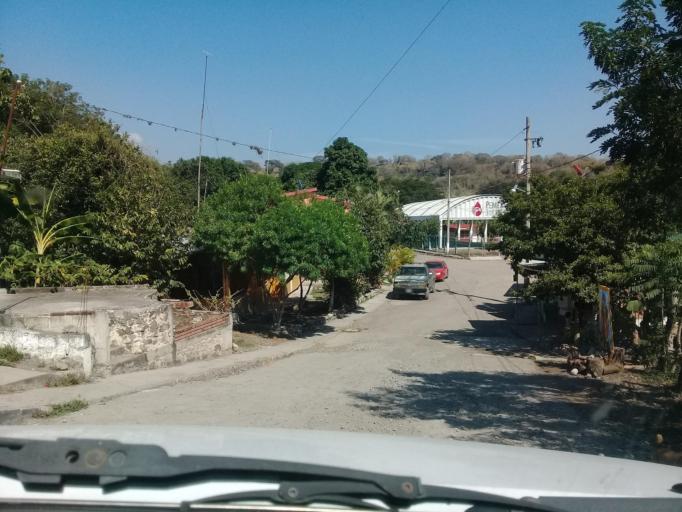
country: MX
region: Veracruz
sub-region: Emiliano Zapata
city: Plan del Rio
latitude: 19.4272
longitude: -96.6129
